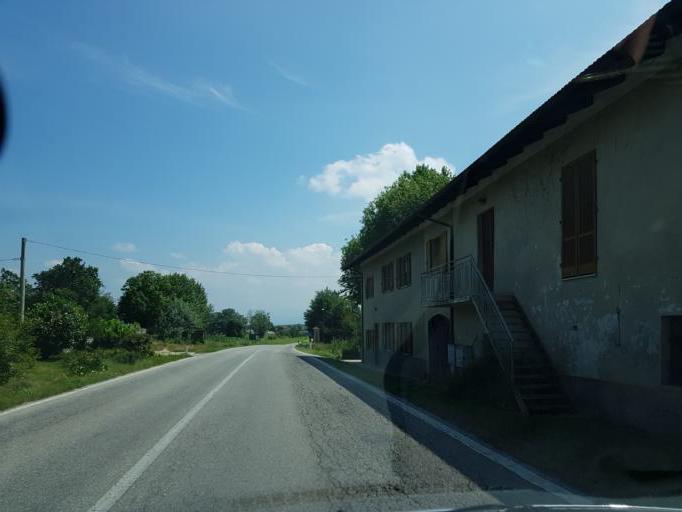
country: IT
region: Piedmont
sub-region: Provincia di Cuneo
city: Montemale di Cuneo
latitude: 44.4429
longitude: 7.4073
